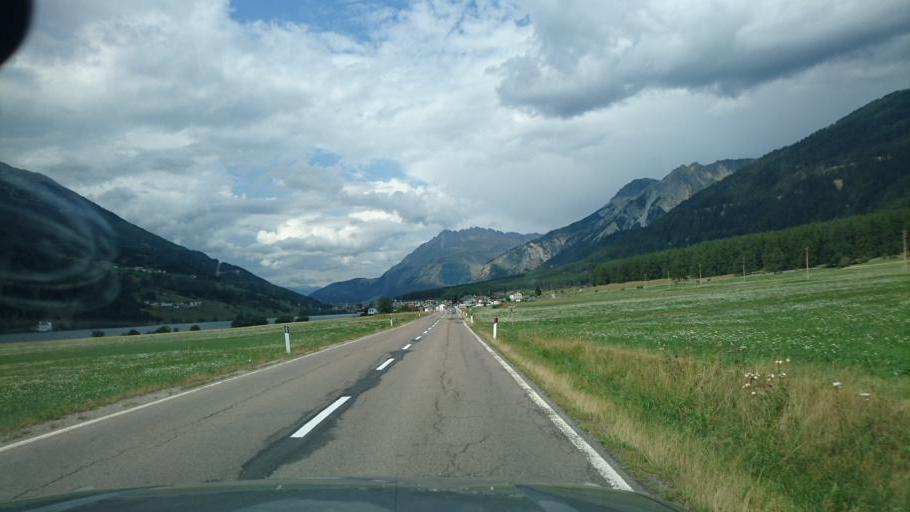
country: IT
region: Trentino-Alto Adige
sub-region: Bolzano
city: Malles Venosta
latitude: 46.7445
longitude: 10.5353
